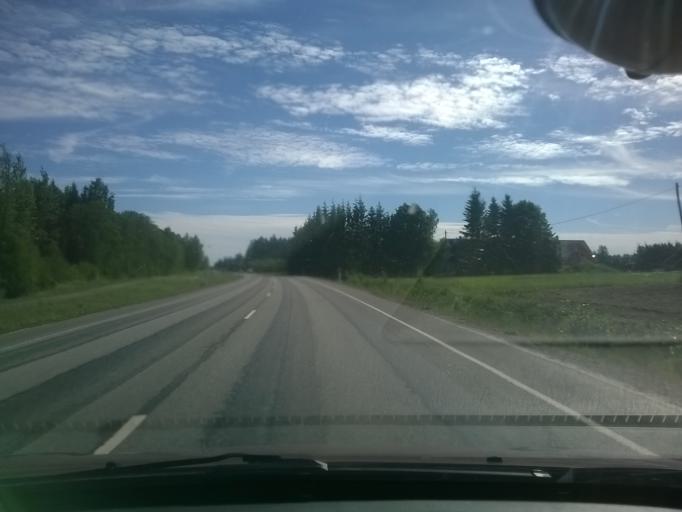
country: EE
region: Jaervamaa
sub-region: Paide linn
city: Paide
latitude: 58.9357
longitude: 25.6351
